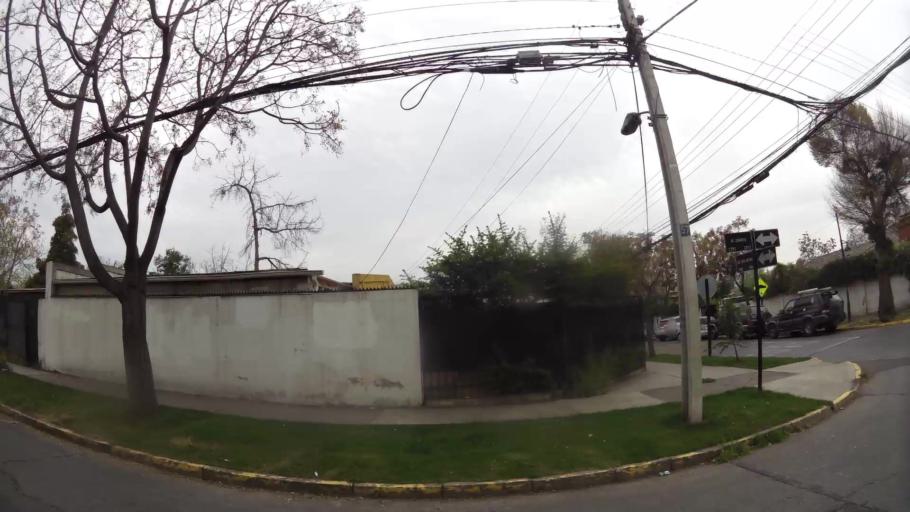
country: CL
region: Santiago Metropolitan
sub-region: Provincia de Santiago
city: Villa Presidente Frei, Nunoa, Santiago, Chile
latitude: -33.4726
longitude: -70.6043
